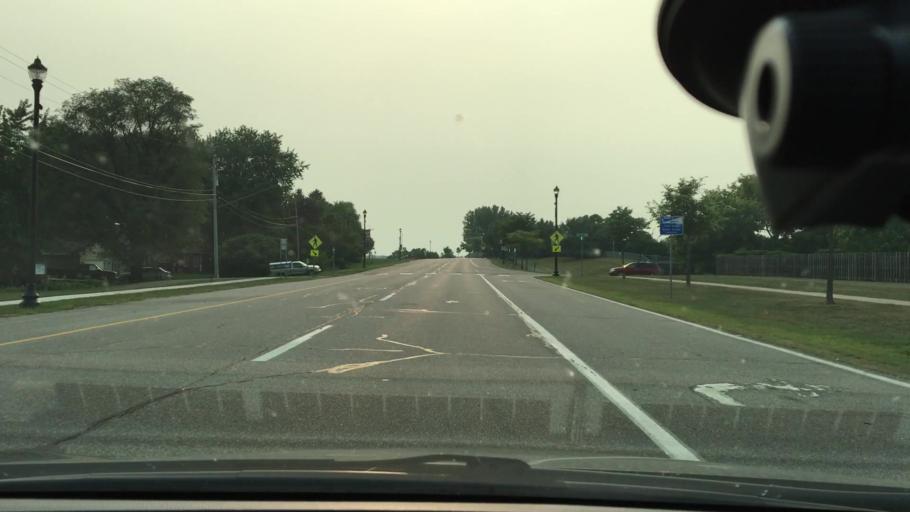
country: US
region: Minnesota
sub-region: Wright County
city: Saint Michael
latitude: 45.2102
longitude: -93.6694
